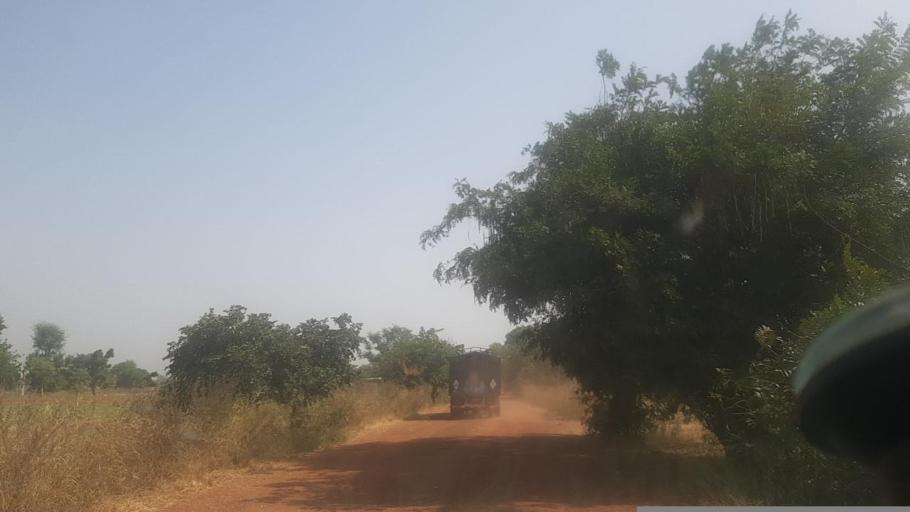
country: ML
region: Segou
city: Bla
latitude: 12.9135
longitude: -6.2476
